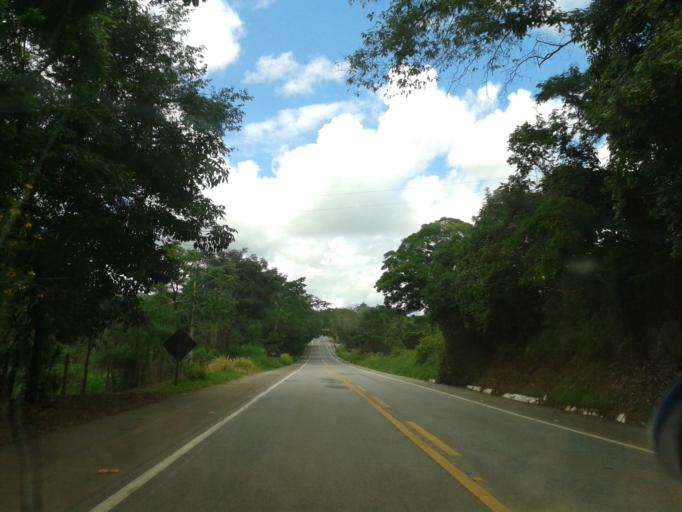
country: BR
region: Goias
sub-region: Goias
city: Goias
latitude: -15.9174
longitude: -50.1277
